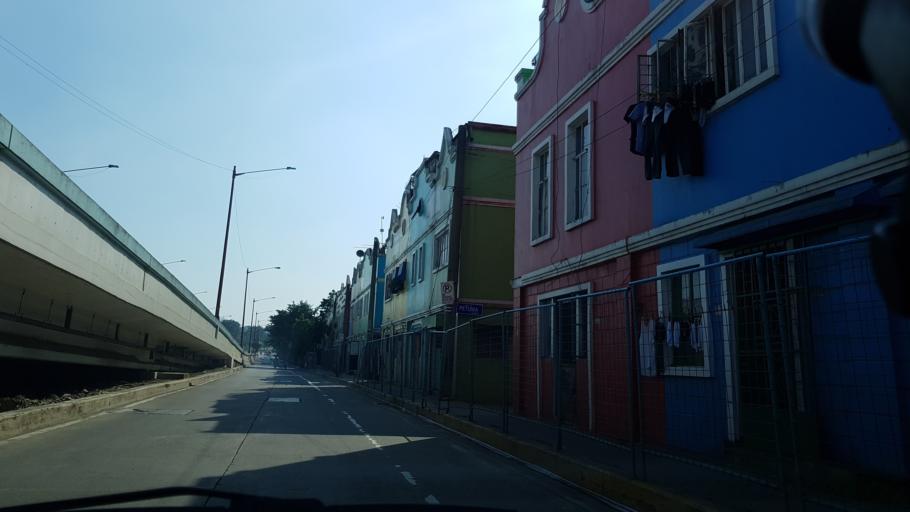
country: PH
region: Metro Manila
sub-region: Marikina
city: Calumpang
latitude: 14.6208
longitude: 121.0799
